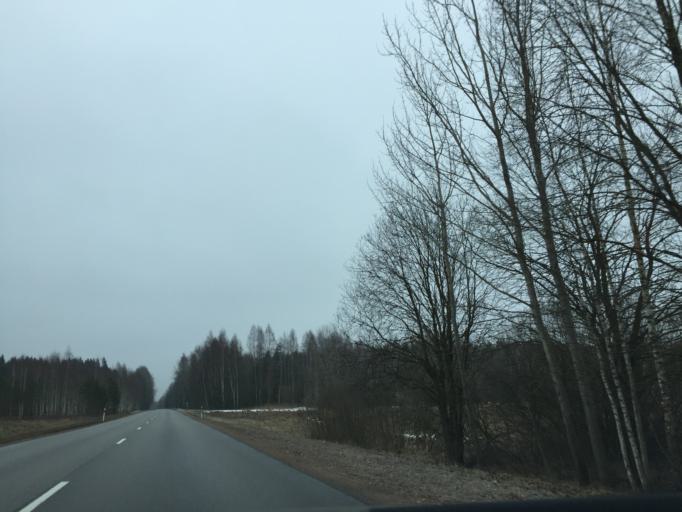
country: LV
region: Lecava
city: Iecava
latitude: 56.6126
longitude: 24.0289
